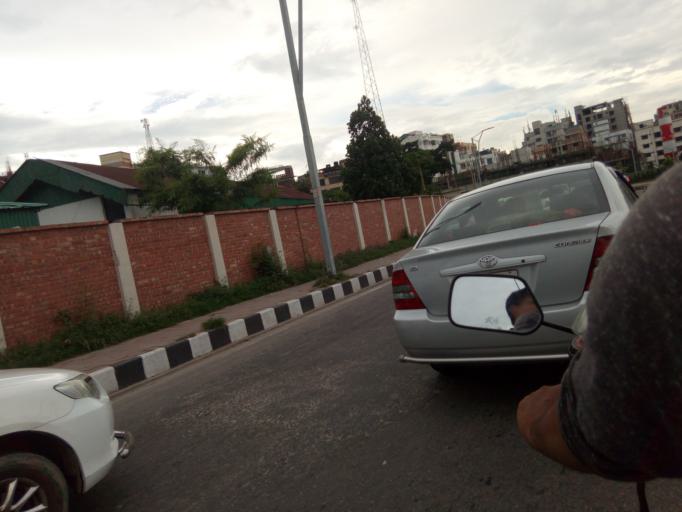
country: BD
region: Dhaka
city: Paltan
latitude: 23.7708
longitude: 90.4128
